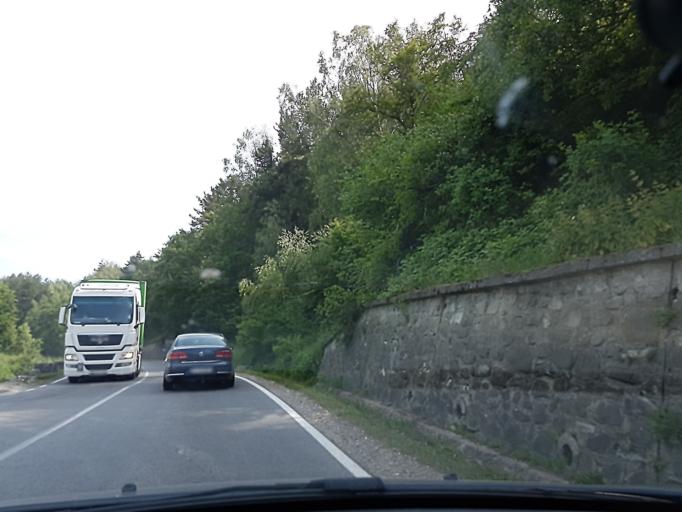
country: RO
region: Prahova
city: Maneciu
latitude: 45.3319
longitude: 25.9692
